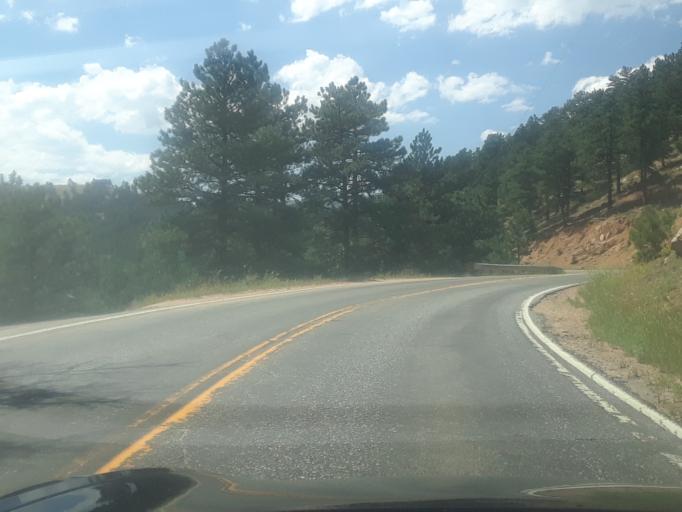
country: US
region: Colorado
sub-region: Boulder County
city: Boulder
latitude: 40.0455
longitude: -105.3313
